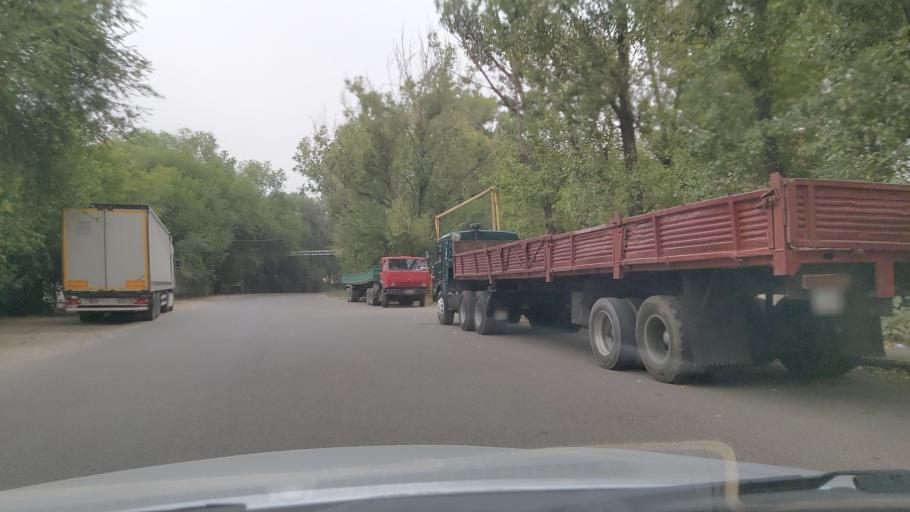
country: KZ
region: Almaty Oblysy
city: Pervomayskiy
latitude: 43.3506
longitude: 76.9746
